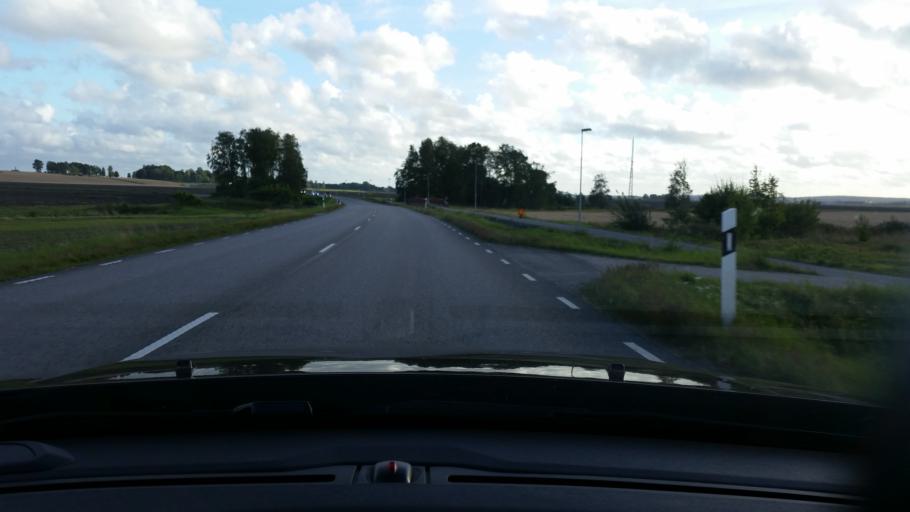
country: SE
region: Vaestra Goetaland
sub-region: Vanersborgs Kommun
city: Vargon
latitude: 58.3389
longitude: 12.3784
